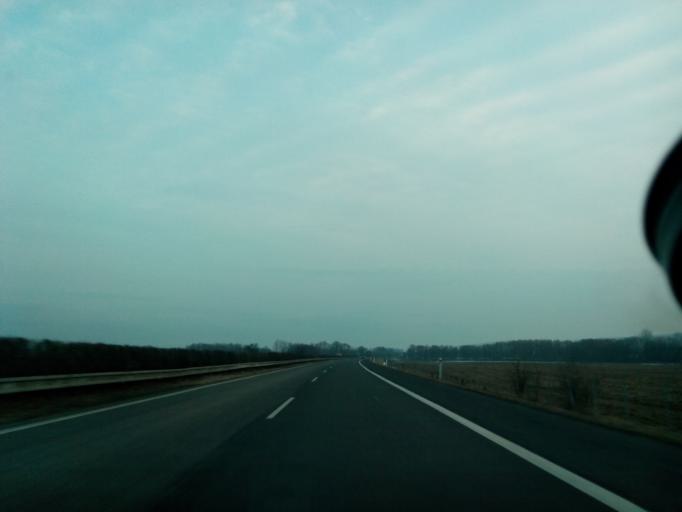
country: SK
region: Kosicky
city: Kosice
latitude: 48.8249
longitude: 21.3095
